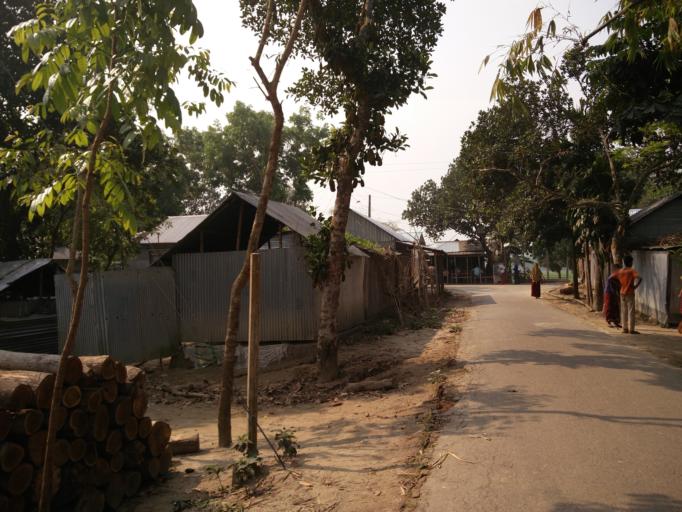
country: BD
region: Dhaka
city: Sherpur
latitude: 24.9111
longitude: 90.1559
